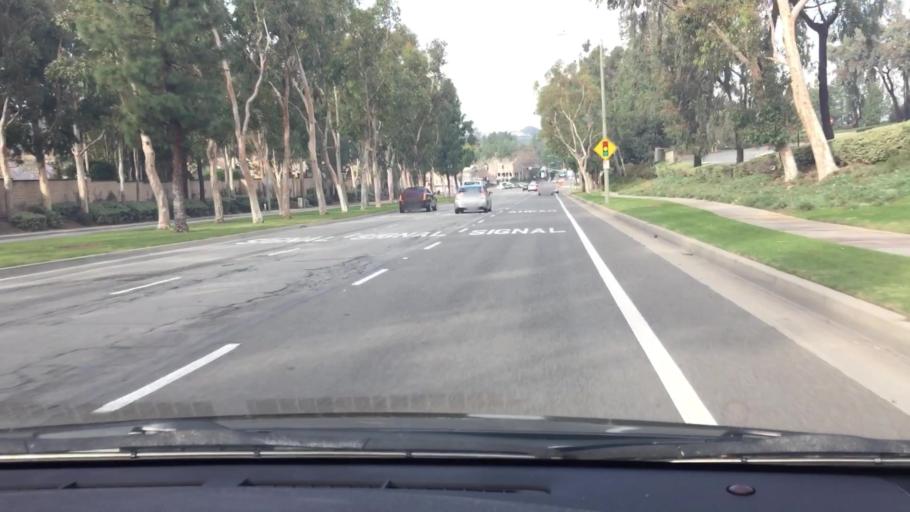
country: US
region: California
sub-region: Orange County
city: North Tustin
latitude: 33.7944
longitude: -117.7686
